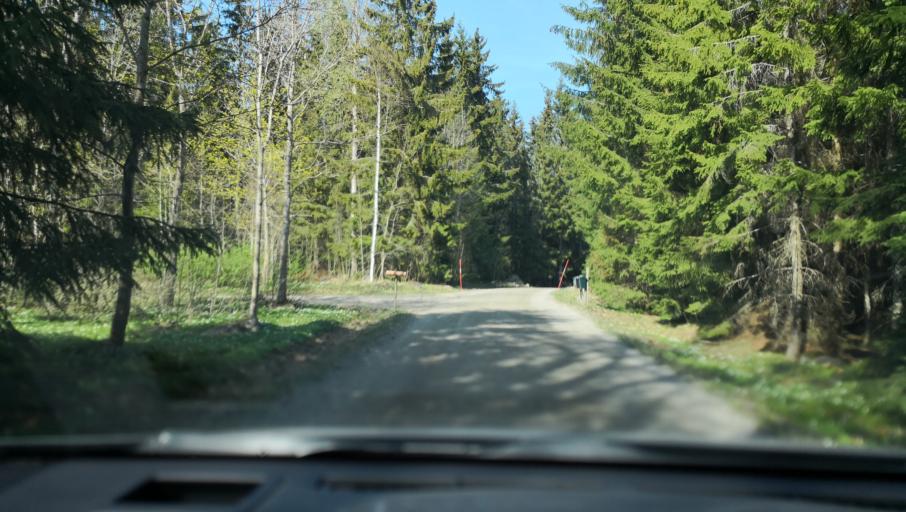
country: SE
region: Uppsala
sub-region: Heby Kommun
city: Heby
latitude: 60.0128
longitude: 16.7375
